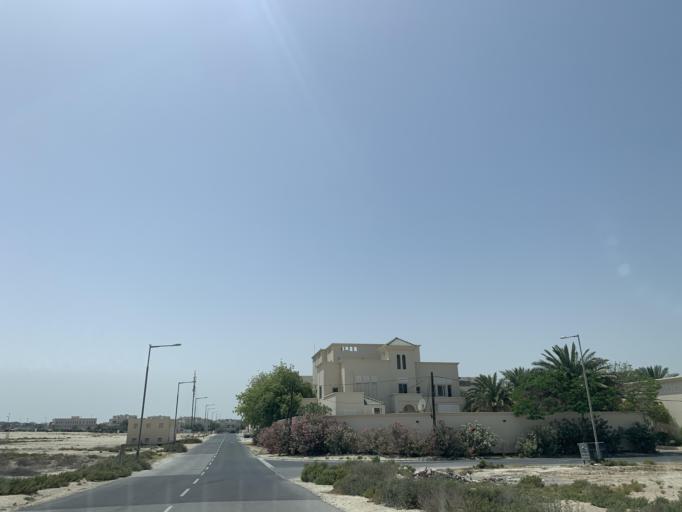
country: BH
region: Northern
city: Ar Rifa'
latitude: 26.1469
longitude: 50.5477
